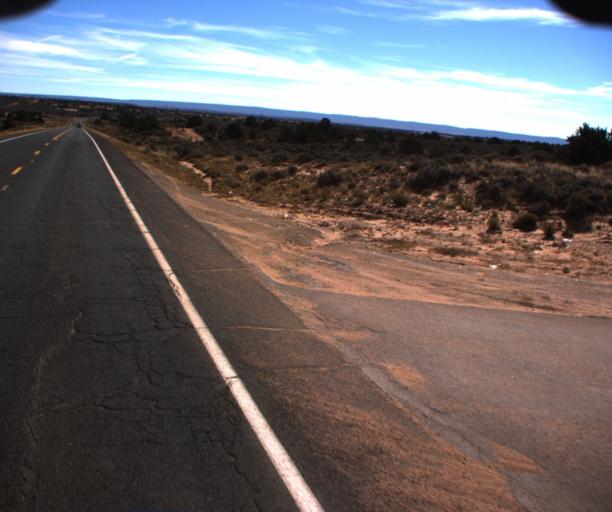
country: US
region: Arizona
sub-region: Coconino County
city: Kaibito
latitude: 36.5782
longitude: -110.7816
